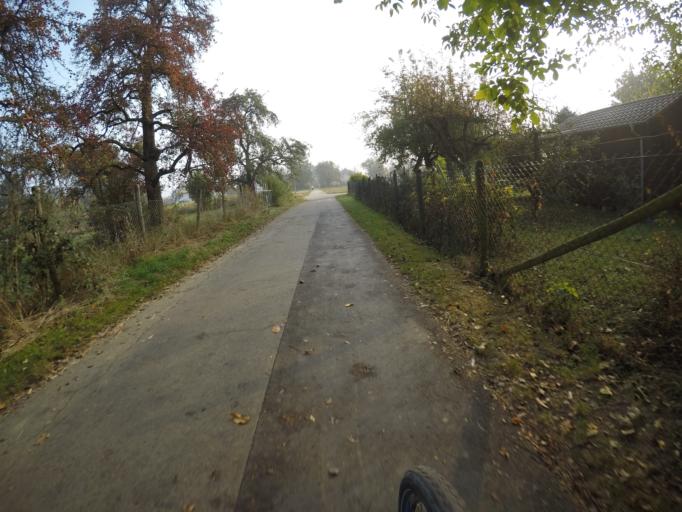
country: DE
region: Baden-Wuerttemberg
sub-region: Regierungsbezirk Stuttgart
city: Leinfelden-Echterdingen
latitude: 48.7379
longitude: 9.1418
